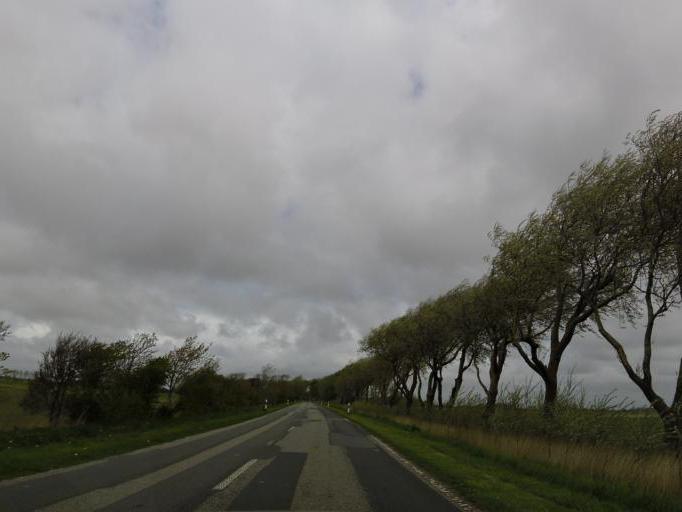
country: DE
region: Schleswig-Holstein
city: Galmsbull
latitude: 54.7648
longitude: 8.7520
